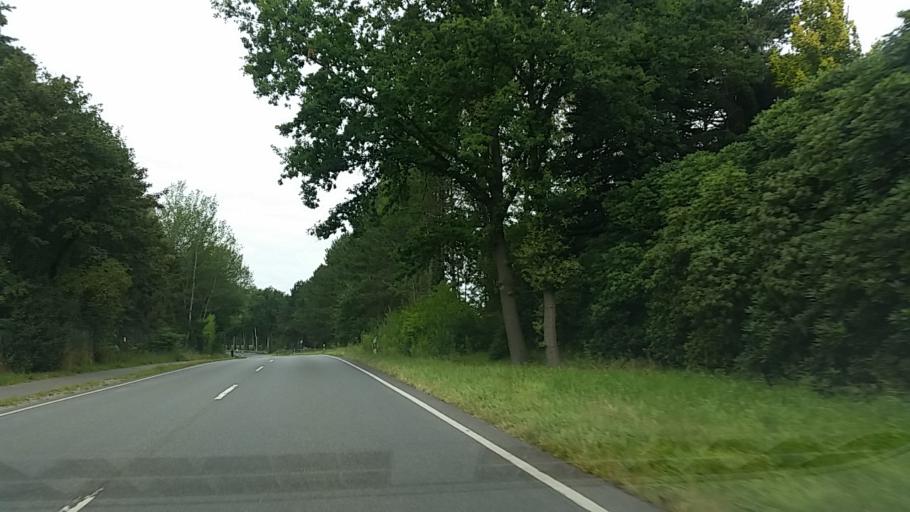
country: DE
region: Lower Saxony
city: Beverstedt
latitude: 53.4294
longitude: 8.8615
